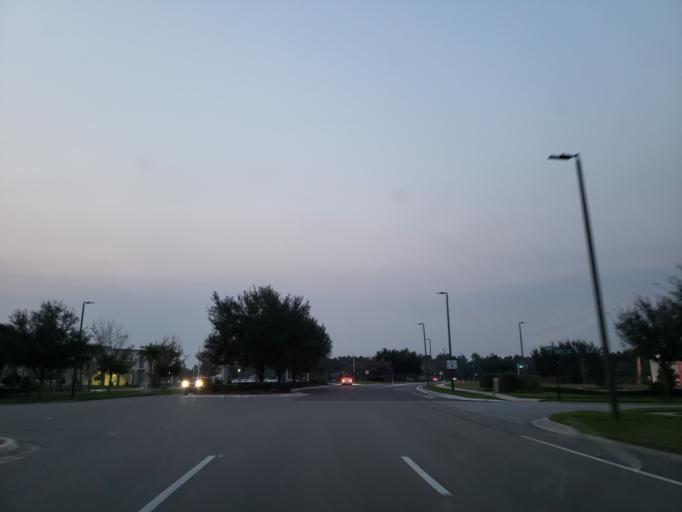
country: US
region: Florida
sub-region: Hillsborough County
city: Bloomingdale
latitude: 27.8521
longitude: -82.2551
